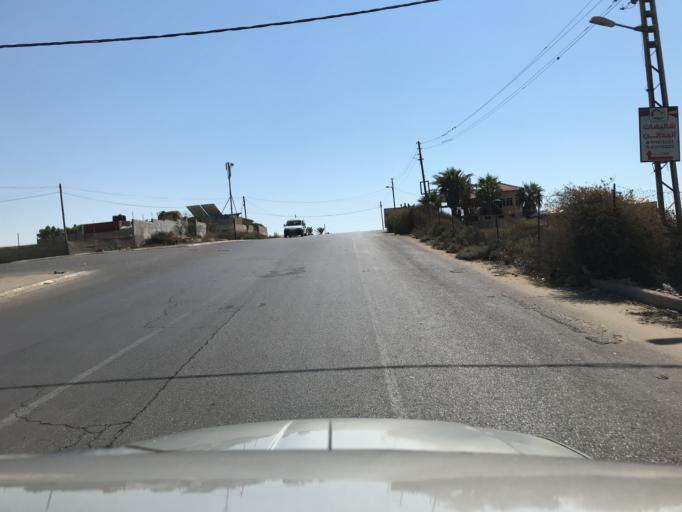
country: PS
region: Gaza Strip
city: Az Zuwaydah
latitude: 31.4575
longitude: 34.3704
